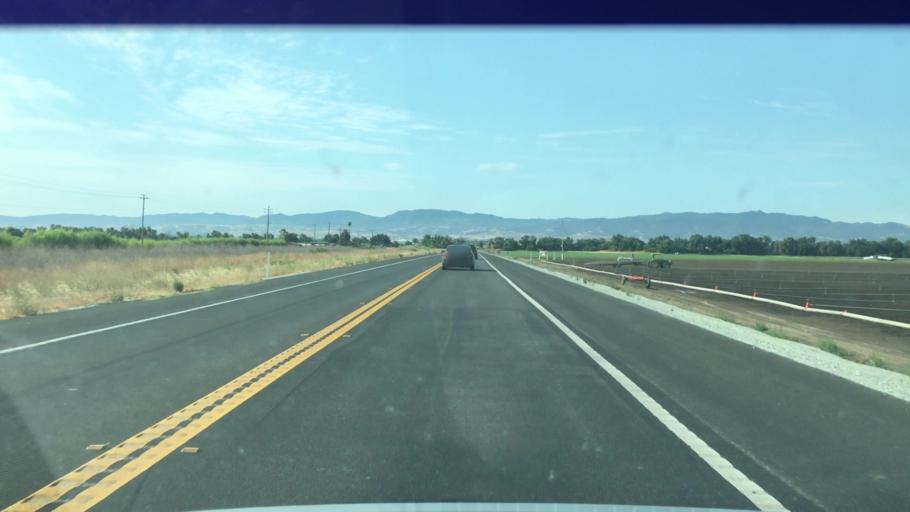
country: US
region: California
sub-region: San Benito County
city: Hollister
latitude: 36.9244
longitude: -121.3906
